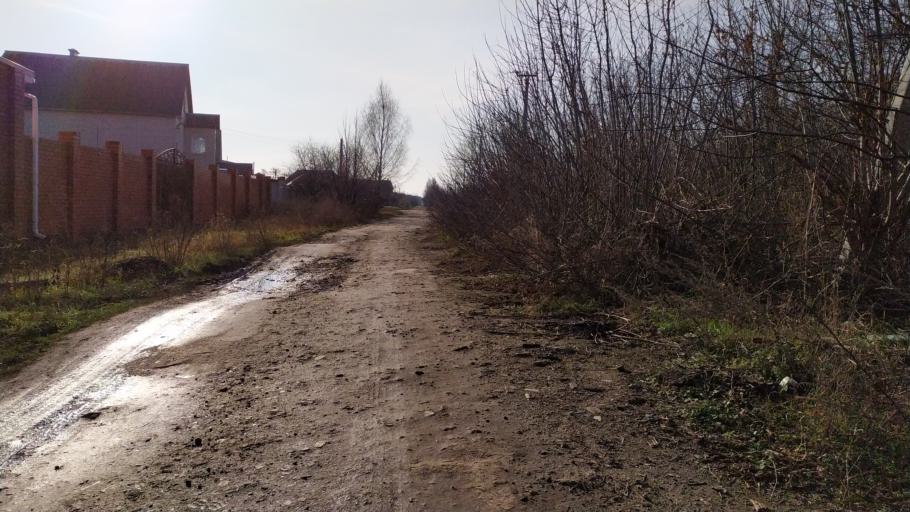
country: RU
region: Kursk
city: Kursk
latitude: 51.6448
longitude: 36.1327
